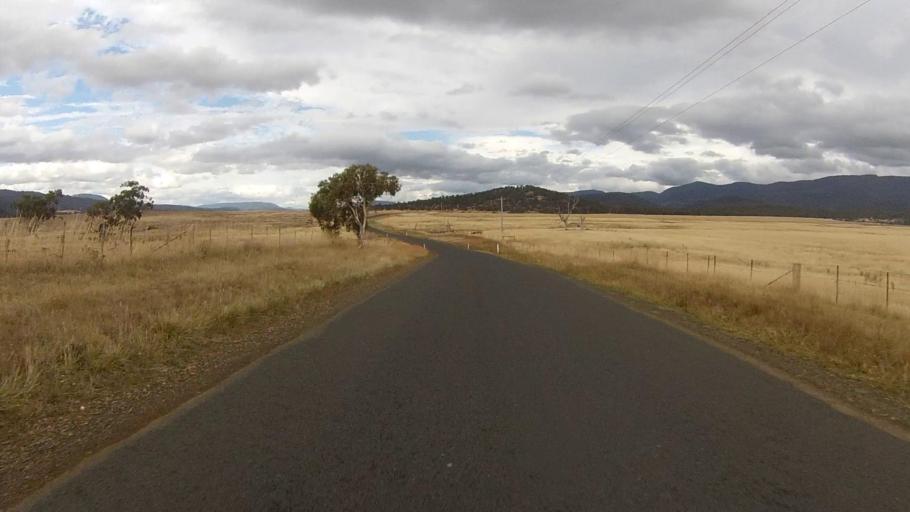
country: AU
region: Tasmania
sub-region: Northern Midlands
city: Evandale
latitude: -41.8263
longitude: 147.7743
